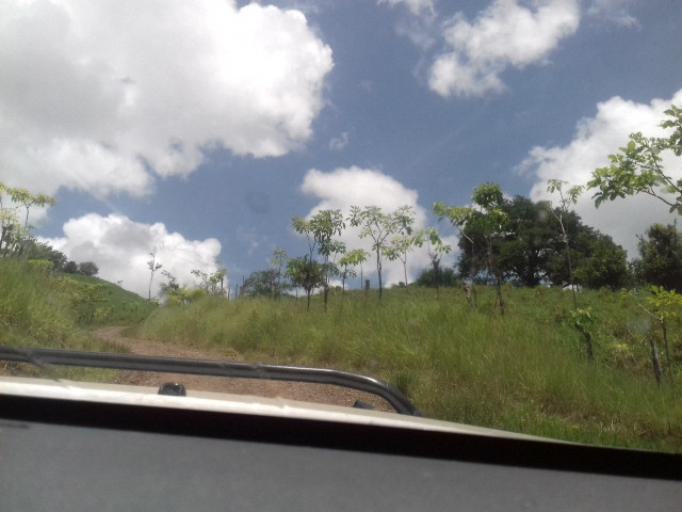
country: NI
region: Matagalpa
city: Rio Blanco
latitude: 12.9903
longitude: -85.3819
